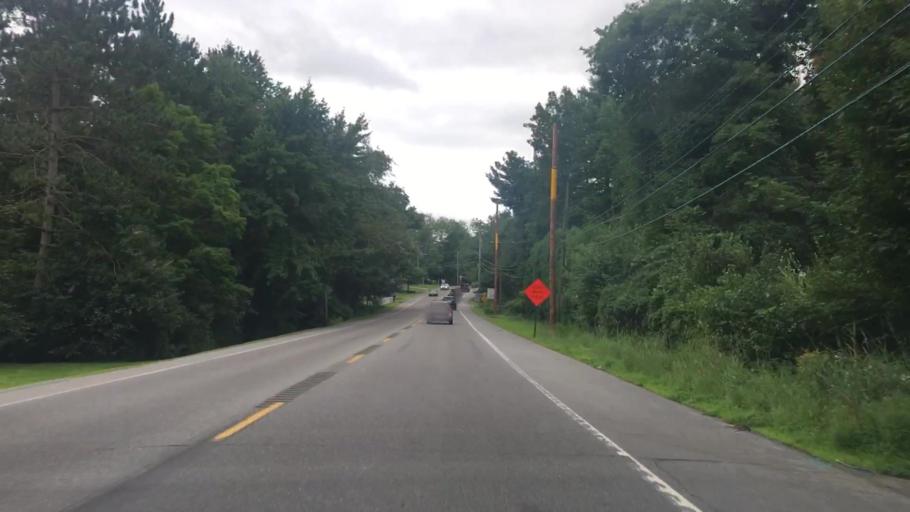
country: US
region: Maine
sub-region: York County
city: Alfred
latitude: 43.4810
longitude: -70.7177
